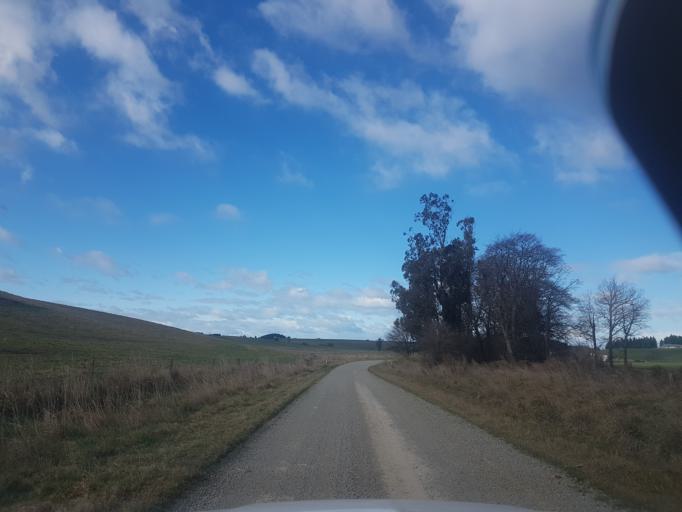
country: NZ
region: Canterbury
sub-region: Timaru District
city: Pleasant Point
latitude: -44.1875
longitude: 171.1917
